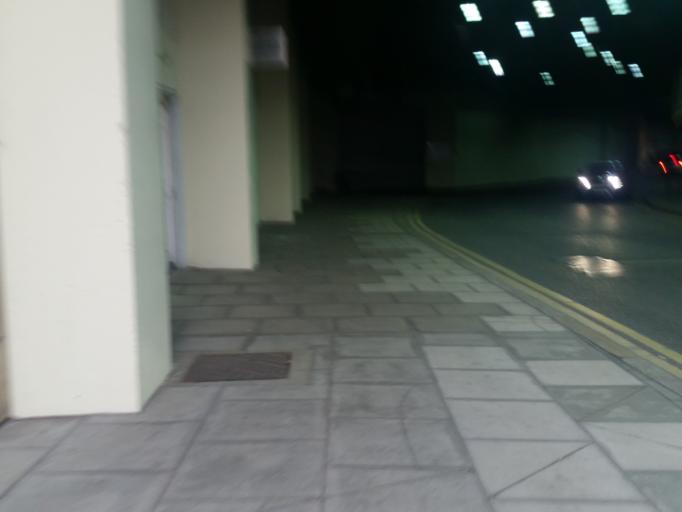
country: GB
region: England
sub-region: Greater London
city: Poplar
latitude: 51.5067
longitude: -0.0252
